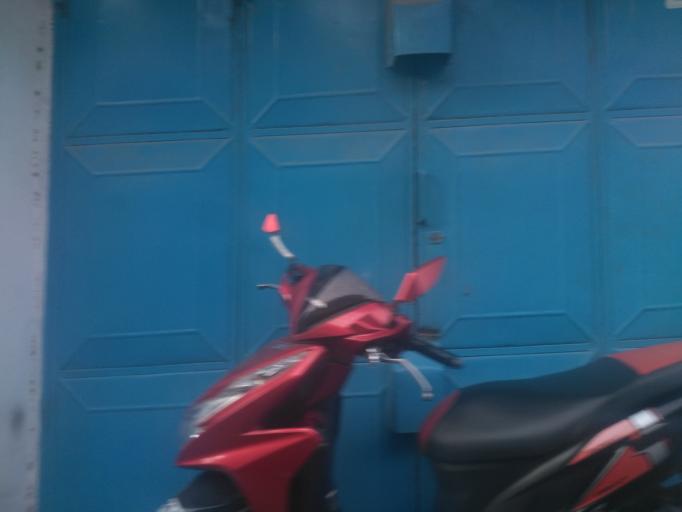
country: TZ
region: Zanzibar Urban/West
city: Zanzibar
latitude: -6.1618
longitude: 39.1968
